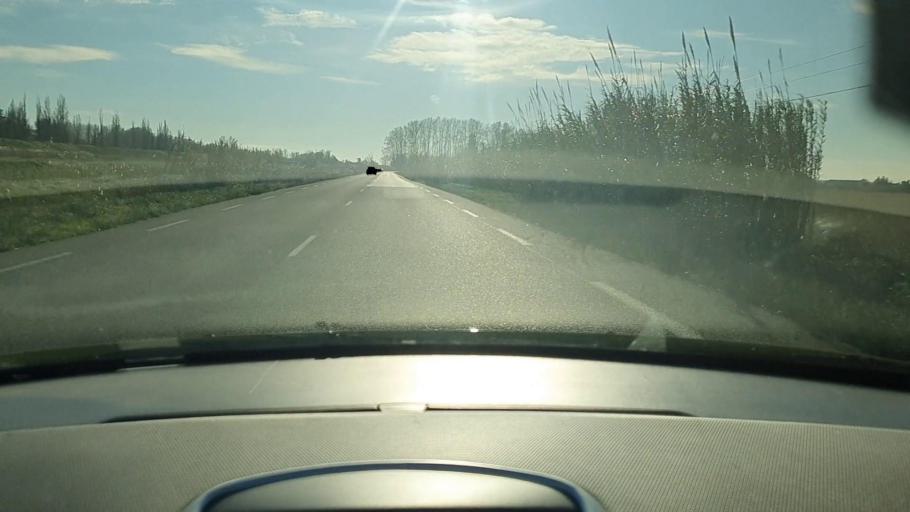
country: FR
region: Languedoc-Roussillon
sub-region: Departement du Gard
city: Fourques
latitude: 43.7329
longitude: 4.6097
